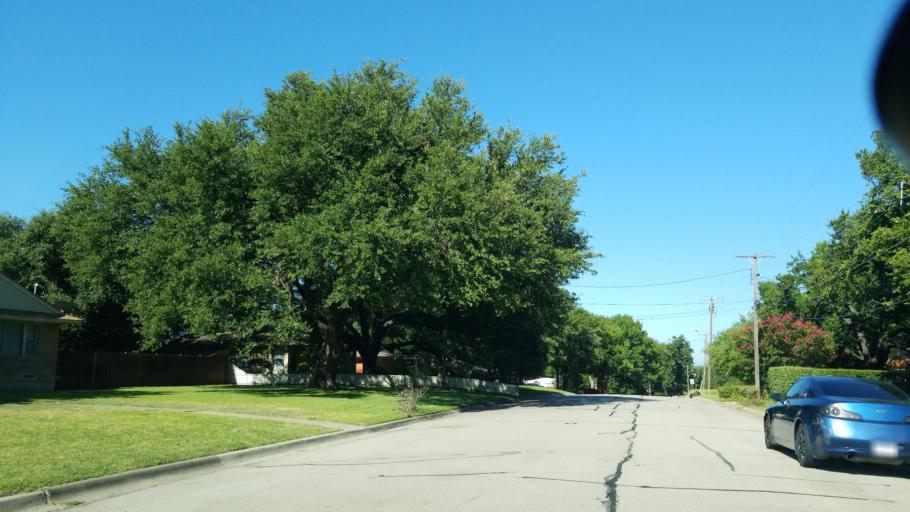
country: US
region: Texas
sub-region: Dallas County
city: Carrollton
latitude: 32.9522
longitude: -96.9004
